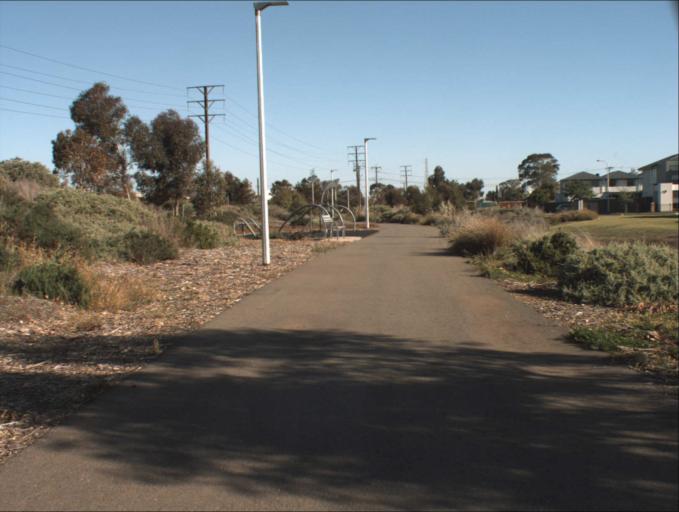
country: AU
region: South Australia
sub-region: Port Adelaide Enfield
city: Birkenhead
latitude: -34.8130
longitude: 138.5074
